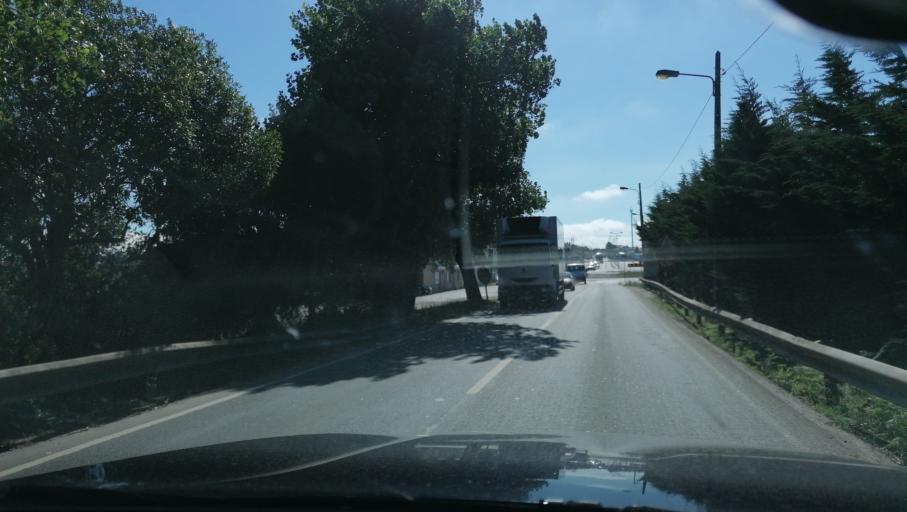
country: PT
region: Aveiro
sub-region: Aveiro
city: Eixo
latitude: 40.6809
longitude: -8.5848
